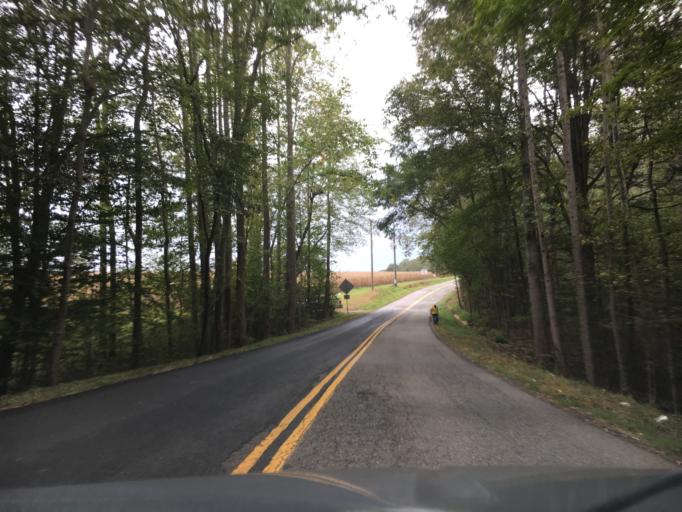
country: US
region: Virginia
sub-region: Amelia County
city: Amelia Court House
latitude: 37.3573
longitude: -77.9737
